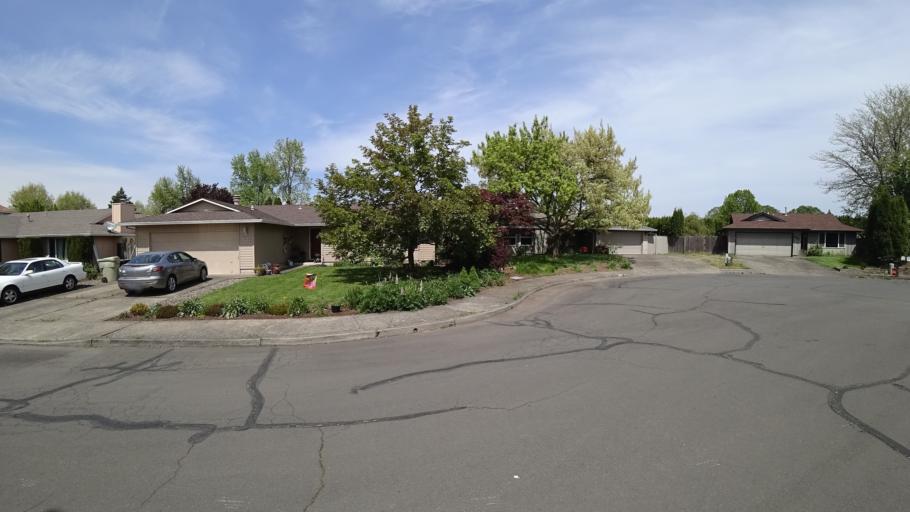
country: US
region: Oregon
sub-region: Washington County
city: Aloha
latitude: 45.5043
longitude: -122.9245
